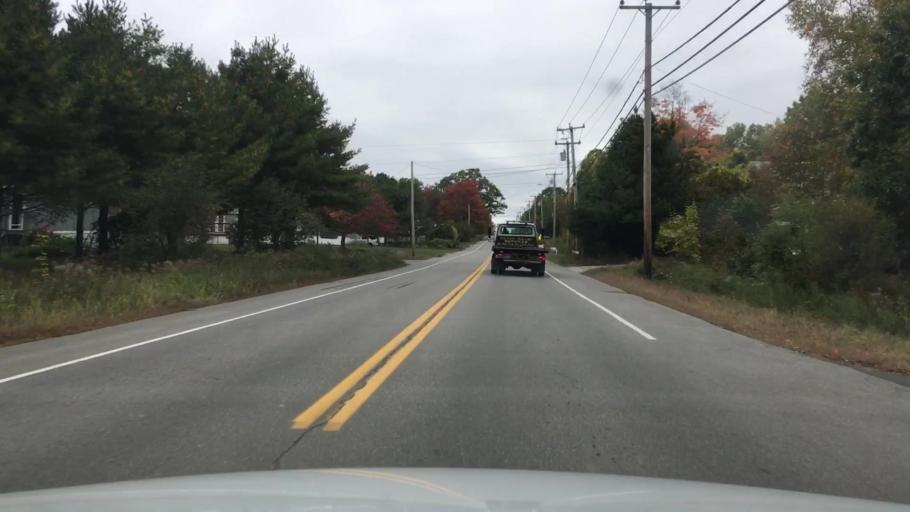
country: US
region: Maine
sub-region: Kennebec County
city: Oakland
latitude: 44.5536
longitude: -69.7322
